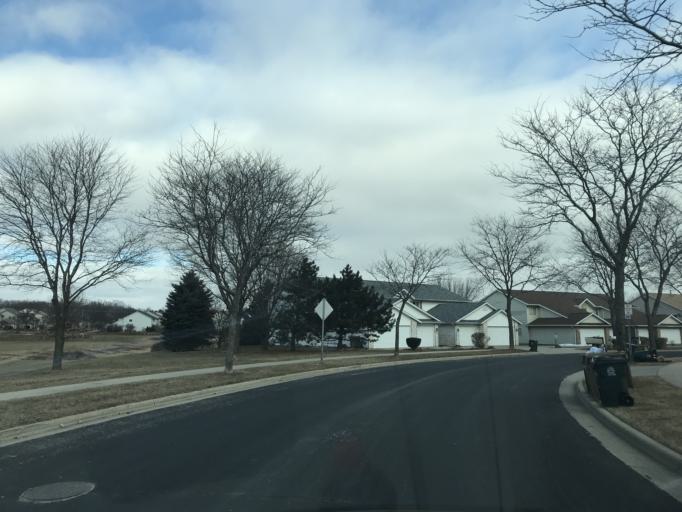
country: US
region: Wisconsin
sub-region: Dane County
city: Monona
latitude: 43.1116
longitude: -89.2993
